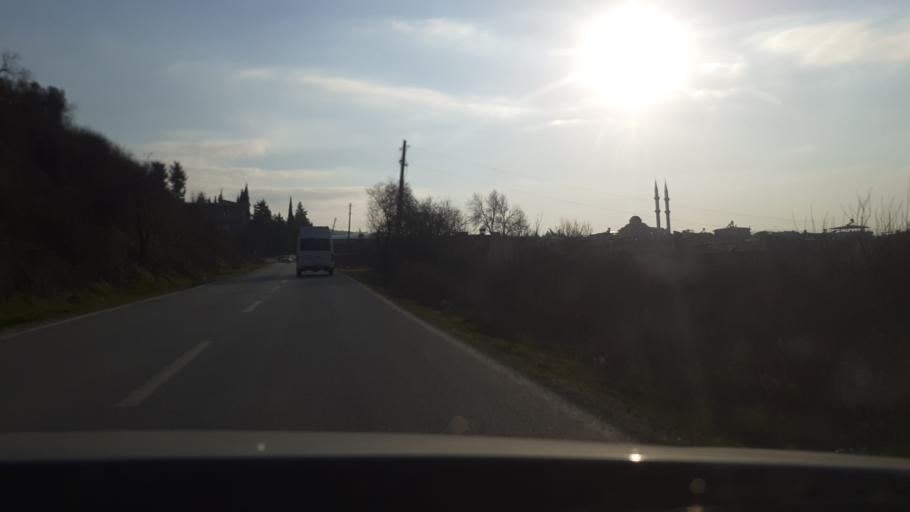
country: TR
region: Hatay
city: Oymakli
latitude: 36.1147
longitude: 36.3019
